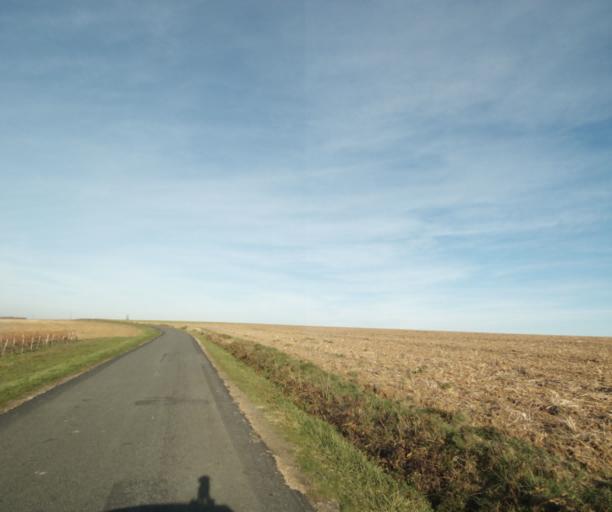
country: FR
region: Poitou-Charentes
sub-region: Departement de la Charente-Maritime
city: Chaniers
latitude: 45.7173
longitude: -0.5290
